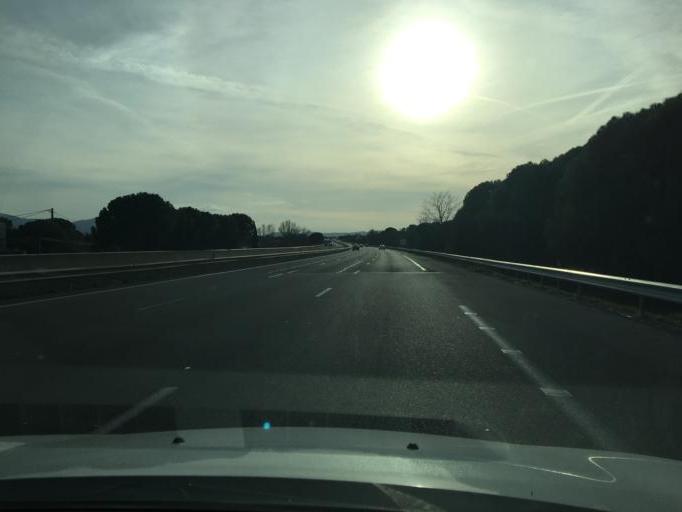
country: FR
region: Provence-Alpes-Cote d'Azur
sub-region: Departement du Var
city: Vidauban
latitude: 43.4126
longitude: 6.4253
